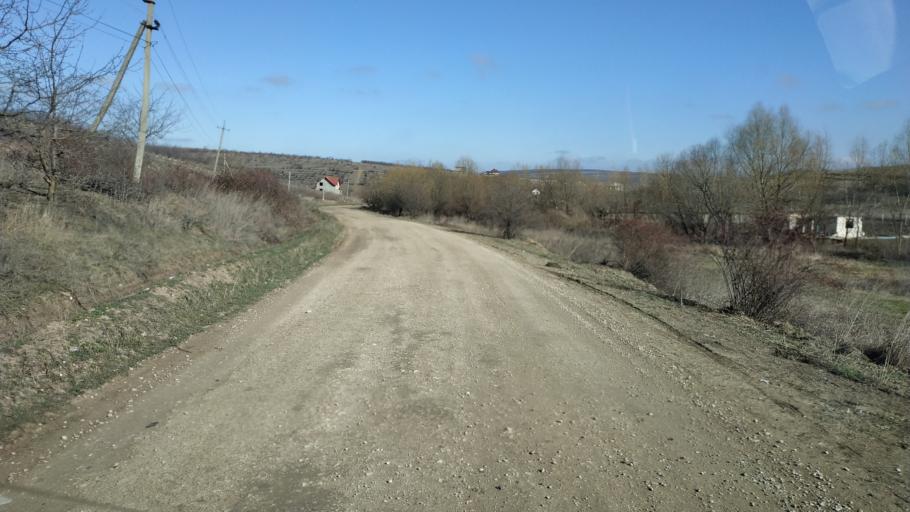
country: MD
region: Hincesti
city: Hincesti
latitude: 46.9249
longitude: 28.6289
